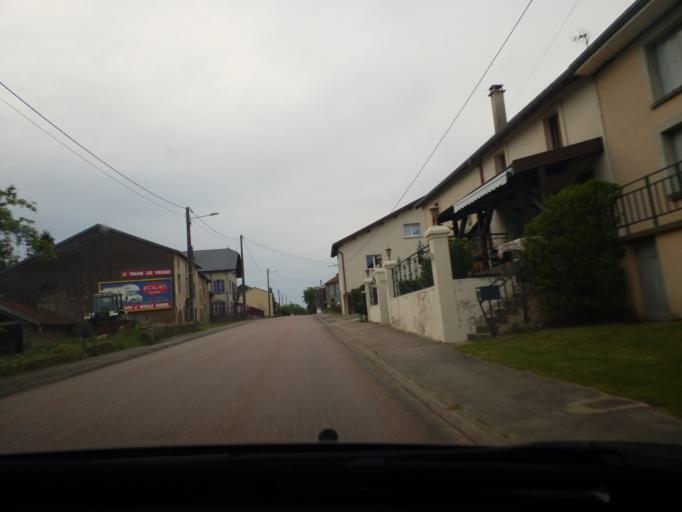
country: FR
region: Lorraine
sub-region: Departement des Vosges
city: Bains-les-Bains
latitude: 48.0347
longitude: 6.1882
